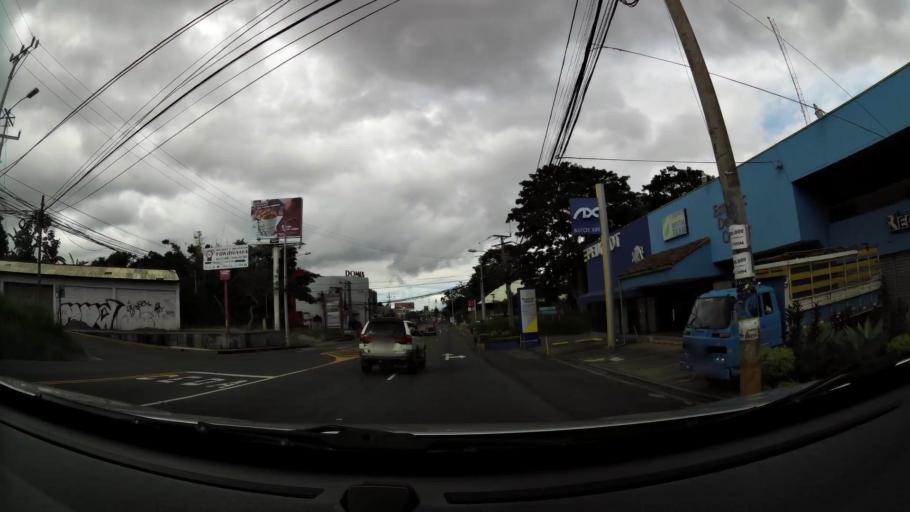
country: CR
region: San Jose
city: Curridabat
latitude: 9.9155
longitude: -84.0313
